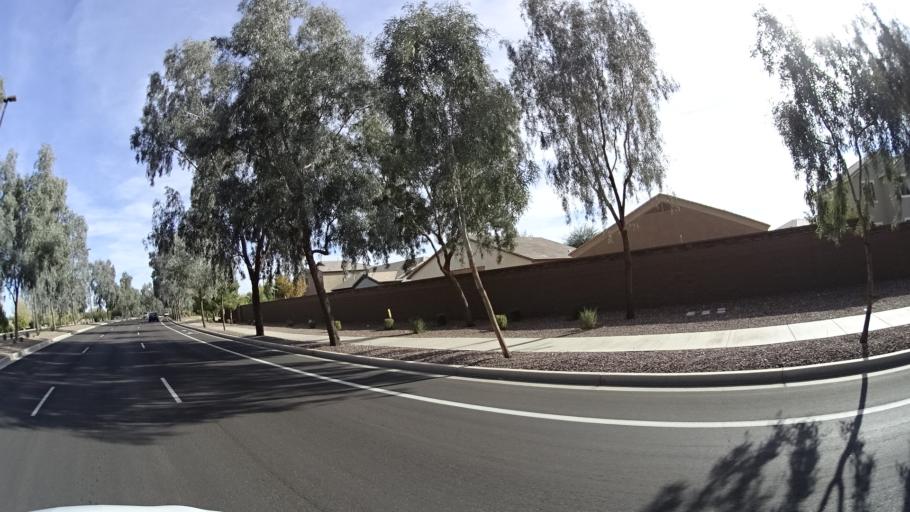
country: US
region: Arizona
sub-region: Maricopa County
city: Queen Creek
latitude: 33.2792
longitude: -111.6959
